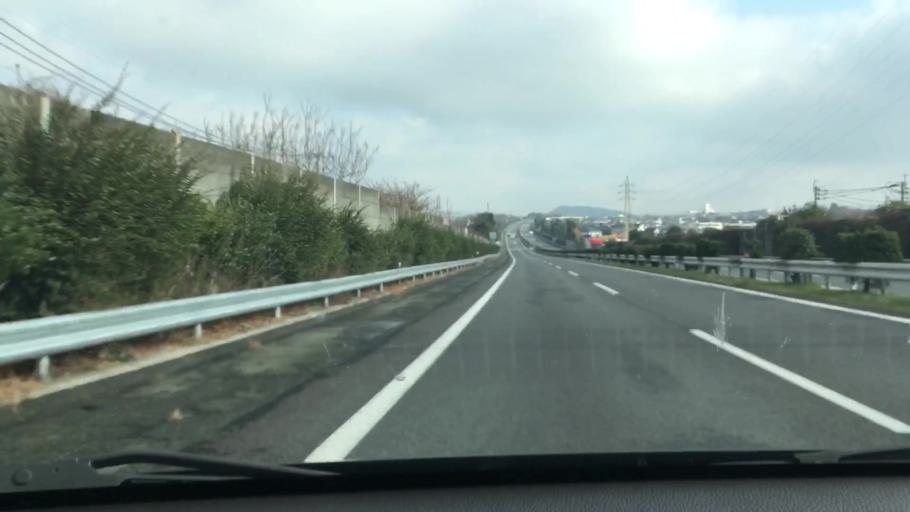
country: JP
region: Kumamoto
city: Ueki
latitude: 32.8597
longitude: 130.7468
